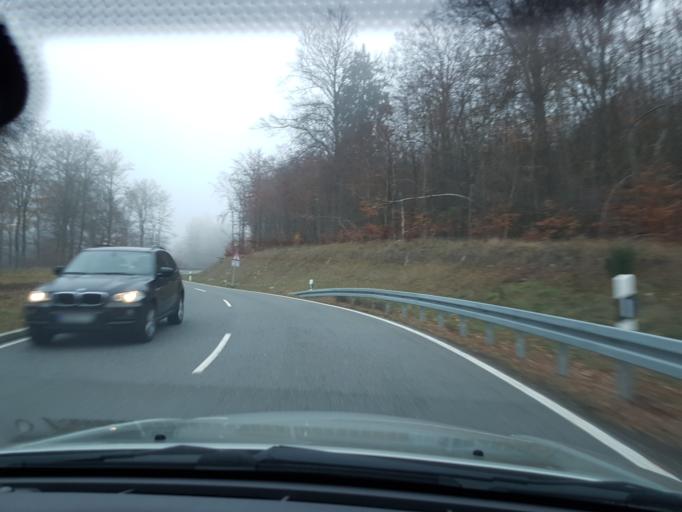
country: DE
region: Hesse
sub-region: Regierungsbezirk Darmstadt
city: Kiedrich
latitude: 50.0748
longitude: 8.0556
